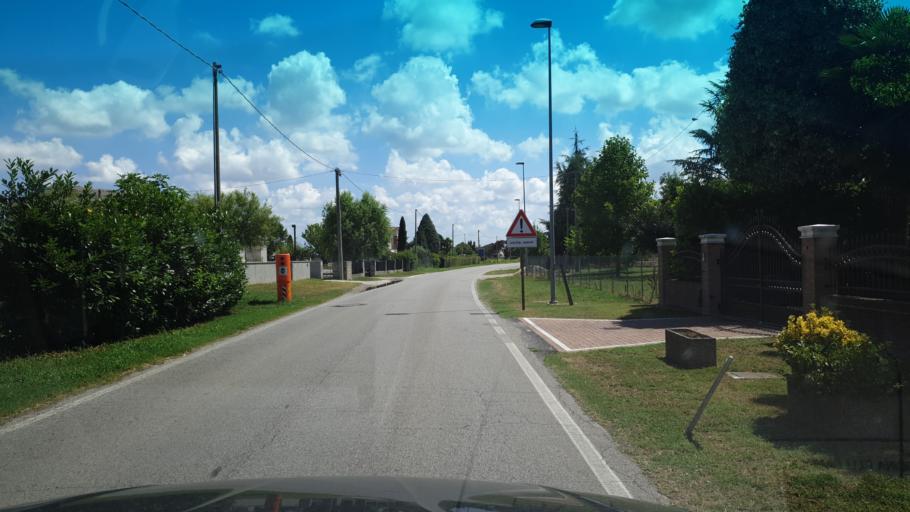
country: IT
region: Veneto
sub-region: Provincia di Rovigo
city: Costa di Rovigo
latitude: 45.0593
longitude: 11.7013
